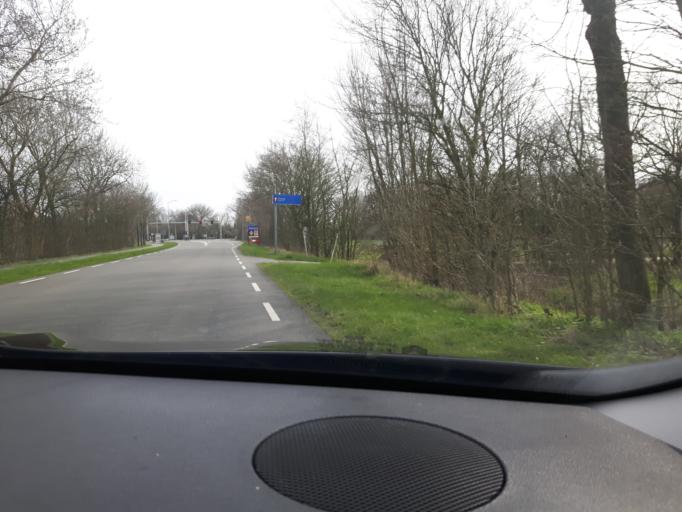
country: NL
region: Zeeland
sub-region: Gemeente Middelburg
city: Middelburg
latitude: 51.5080
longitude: 3.6006
